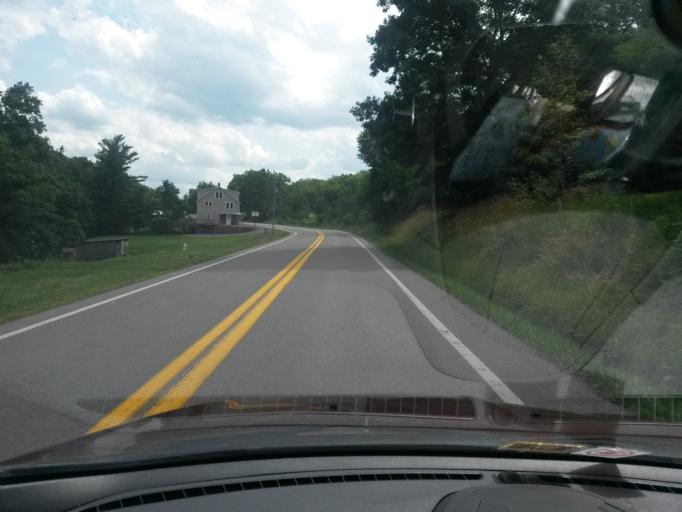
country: US
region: Virginia
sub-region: Highland County
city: Monterey
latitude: 38.5032
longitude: -79.4950
